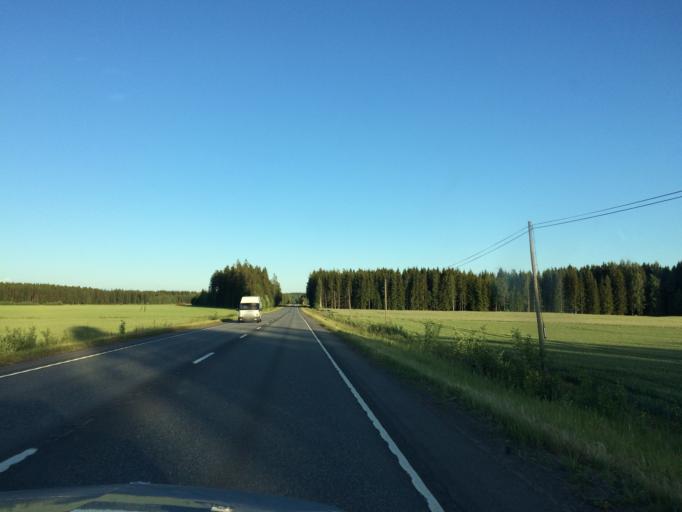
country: FI
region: Haeme
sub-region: Haemeenlinna
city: Tervakoski
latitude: 60.7866
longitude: 24.6813
